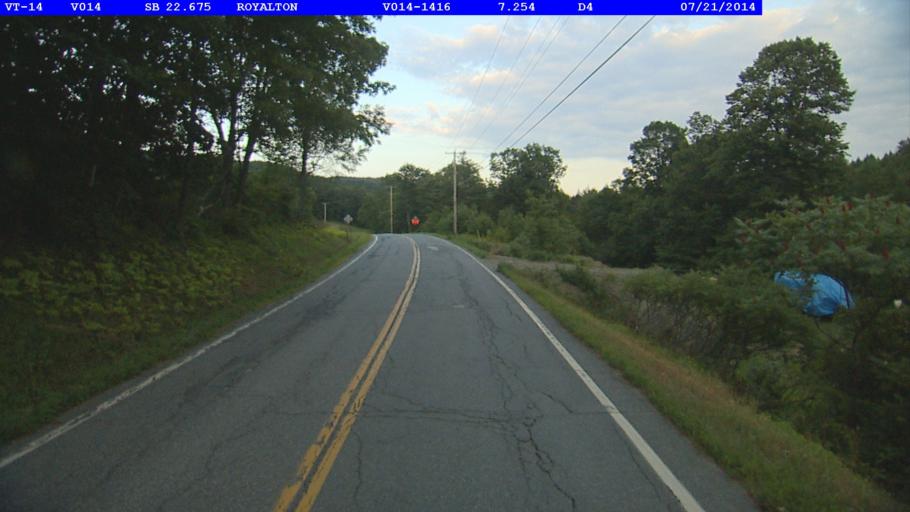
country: US
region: Vermont
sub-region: Orange County
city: Randolph
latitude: 43.8406
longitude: -72.5835
